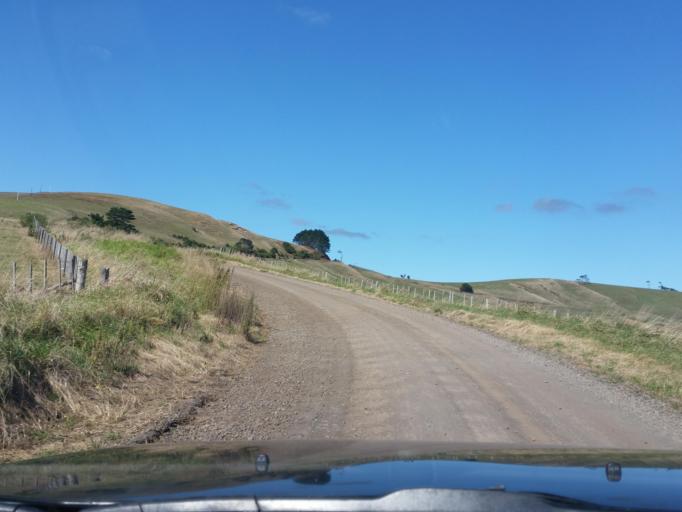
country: NZ
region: Northland
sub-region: Kaipara District
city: Dargaville
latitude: -35.7218
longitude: 173.5640
